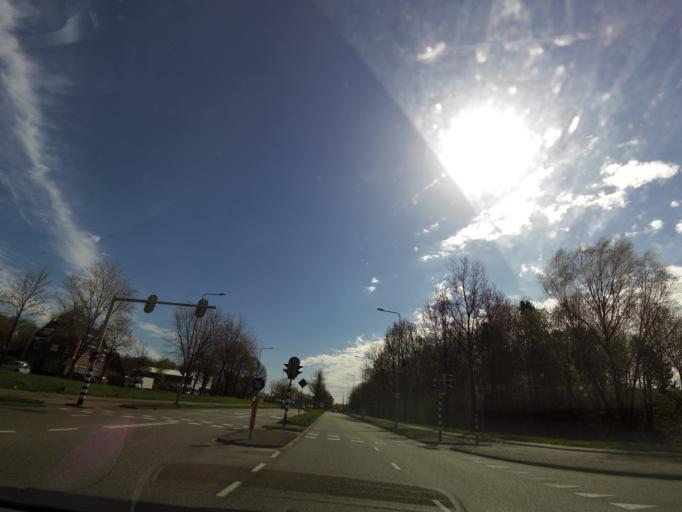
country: NL
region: Limburg
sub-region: Gemeente Heerlen
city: Nieuw-Lotbroek
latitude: 50.9045
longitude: 5.9539
